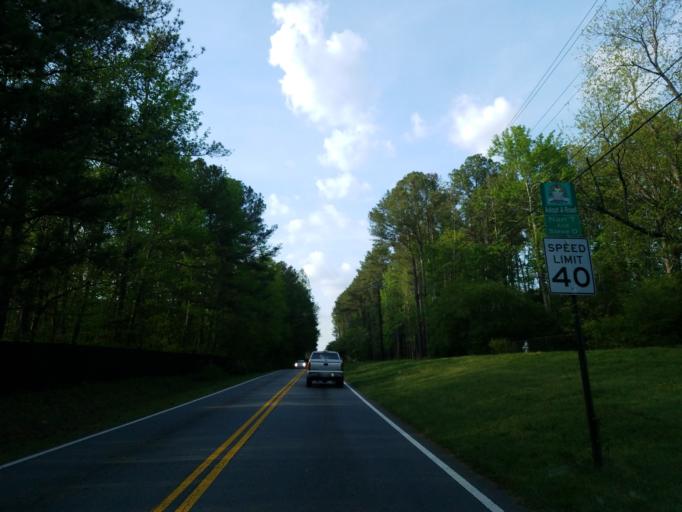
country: US
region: Georgia
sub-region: Fulton County
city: Roswell
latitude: 34.0619
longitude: -84.3610
